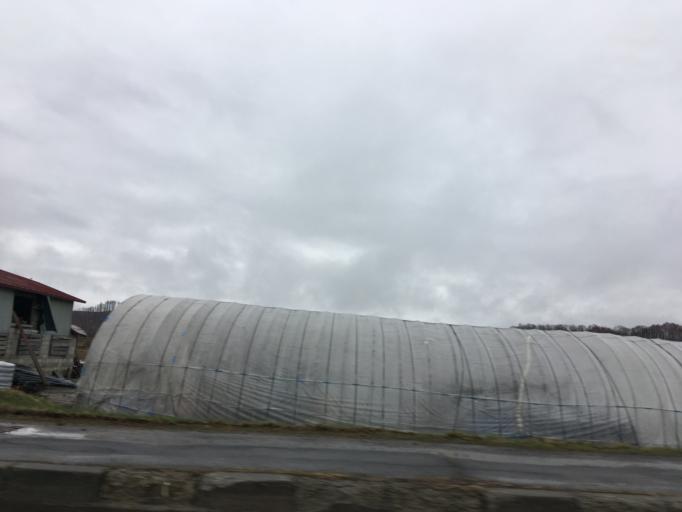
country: JP
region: Hokkaido
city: Nayoro
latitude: 44.0976
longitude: 142.4747
